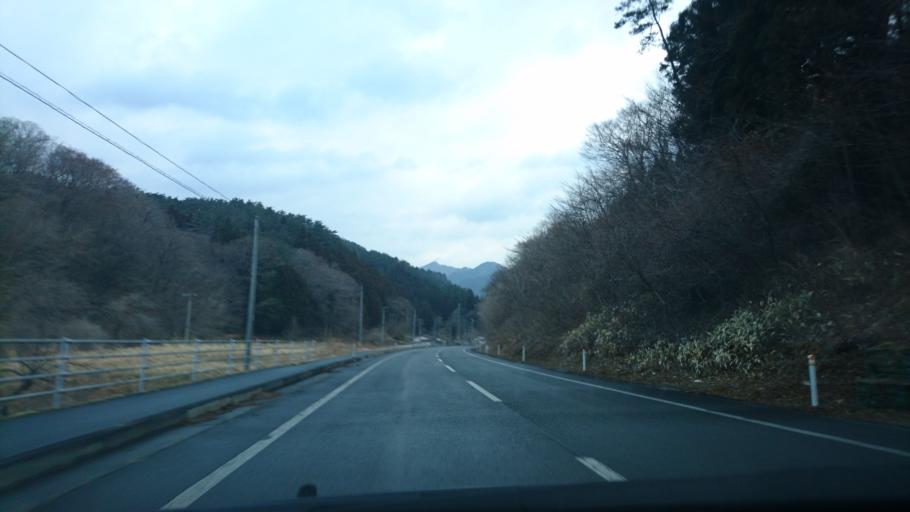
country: JP
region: Iwate
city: Ofunato
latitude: 39.0079
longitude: 141.5445
